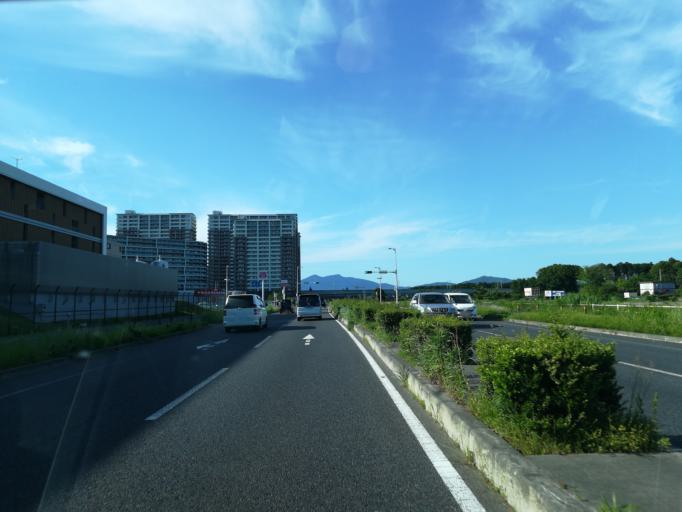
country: JP
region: Ibaraki
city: Naka
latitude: 36.0782
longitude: 140.0857
